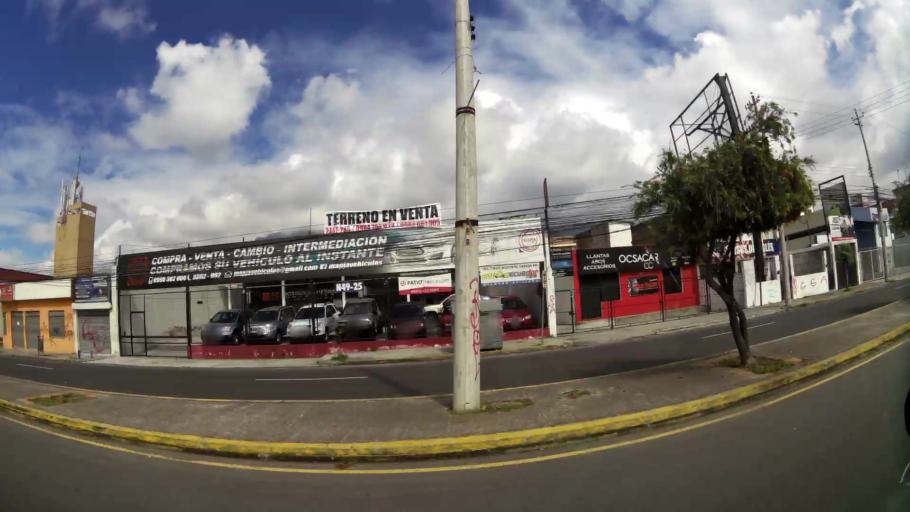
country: EC
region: Pichincha
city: Quito
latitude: -0.1485
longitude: -78.4896
